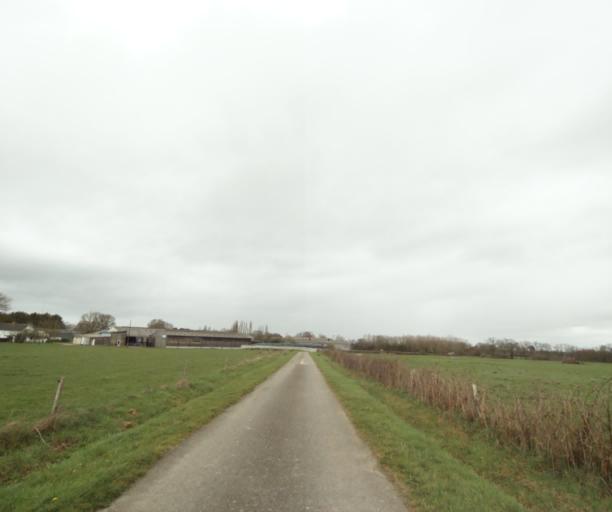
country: FR
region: Pays de la Loire
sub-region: Departement de la Loire-Atlantique
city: Bouvron
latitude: 47.4327
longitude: -1.8474
